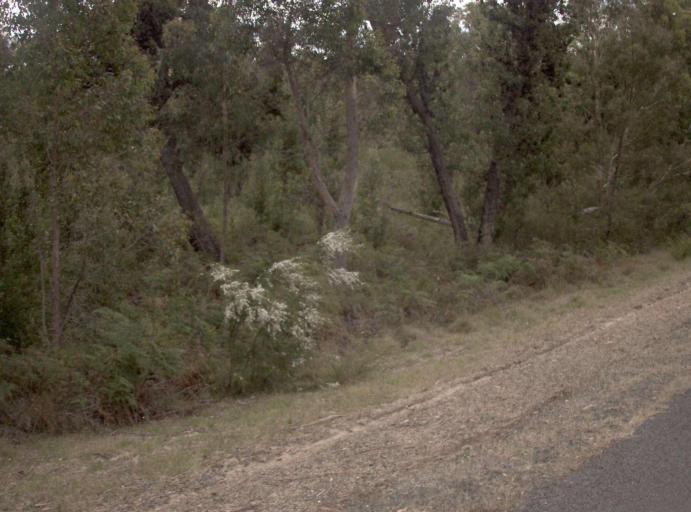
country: AU
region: Victoria
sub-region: Wellington
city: Sale
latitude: -38.3324
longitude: 147.0172
